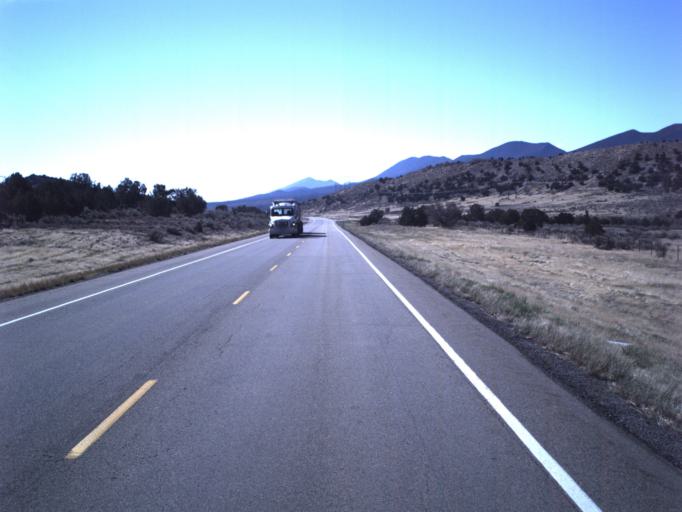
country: US
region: Utah
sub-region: Sanpete County
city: Gunnison
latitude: 39.3695
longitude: -111.9292
